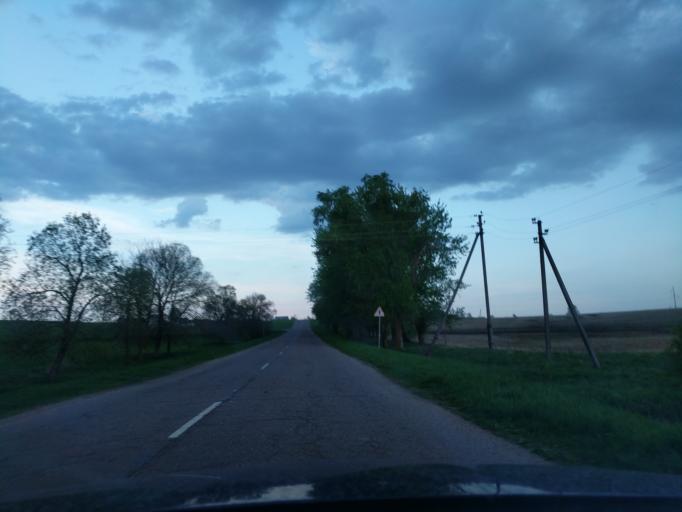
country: BY
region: Minsk
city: Novy Svyerzhan'
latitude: 53.4749
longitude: 26.6343
